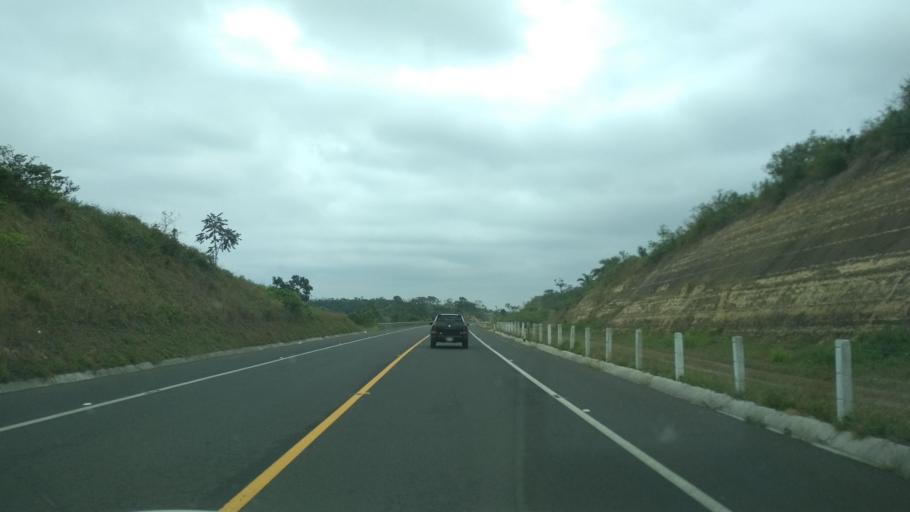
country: MX
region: Veracruz
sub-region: Papantla
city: Polutla
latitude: 20.4445
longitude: -97.2382
